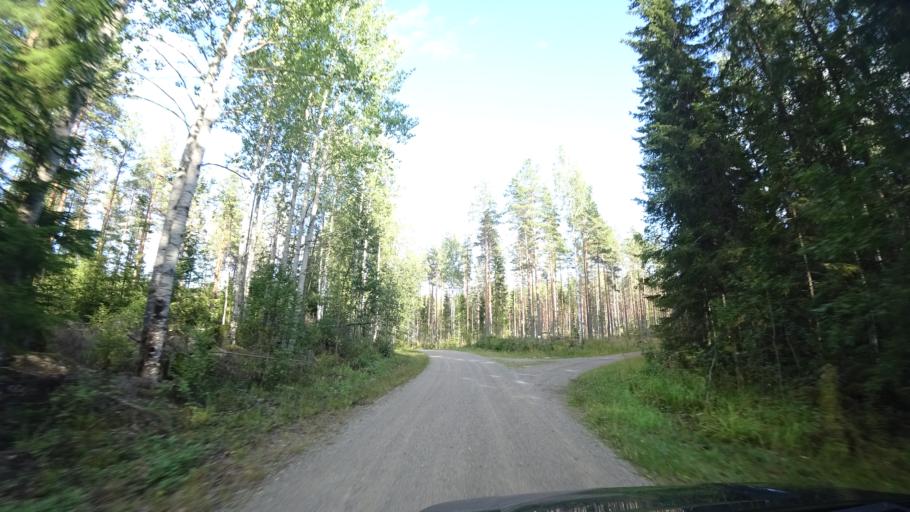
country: FI
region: Paijanne Tavastia
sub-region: Lahti
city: Auttoinen
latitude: 61.2119
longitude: 25.1678
